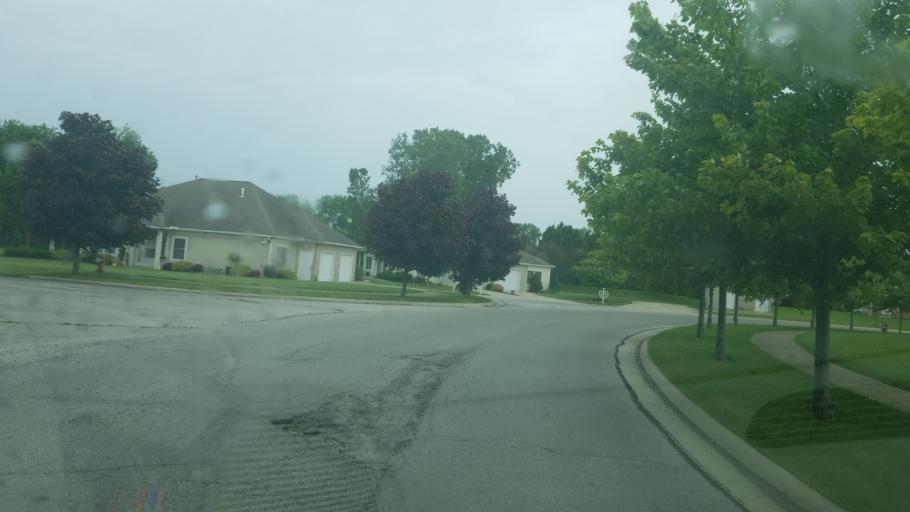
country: US
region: Ohio
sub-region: Crawford County
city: Bucyrus
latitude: 40.7869
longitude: -82.9828
